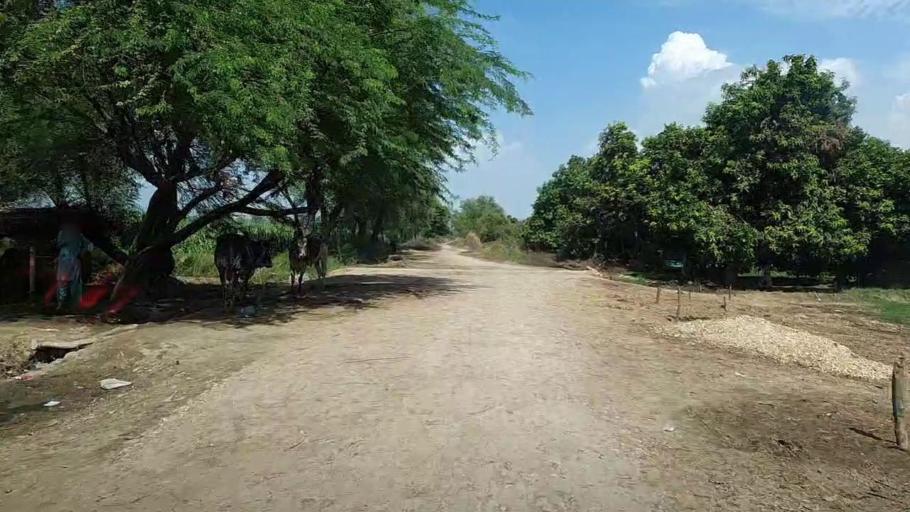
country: PK
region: Sindh
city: Bhiria
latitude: 26.9213
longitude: 68.2231
